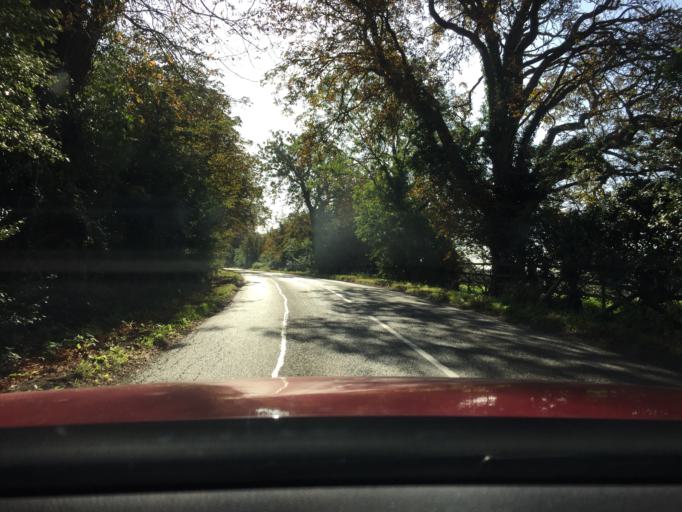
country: GB
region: England
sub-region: Leicestershire
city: Houghton on the Hill
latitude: 52.6548
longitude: -1.0135
